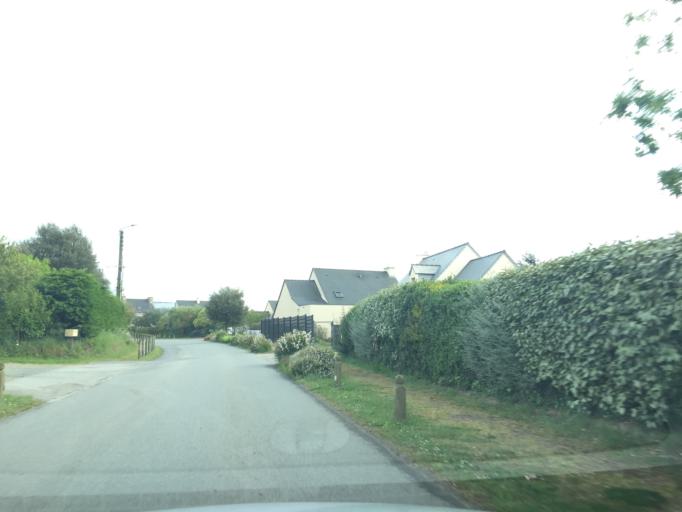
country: FR
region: Brittany
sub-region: Departement des Cotes-d'Armor
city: Crehen
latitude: 48.5787
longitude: -2.1970
